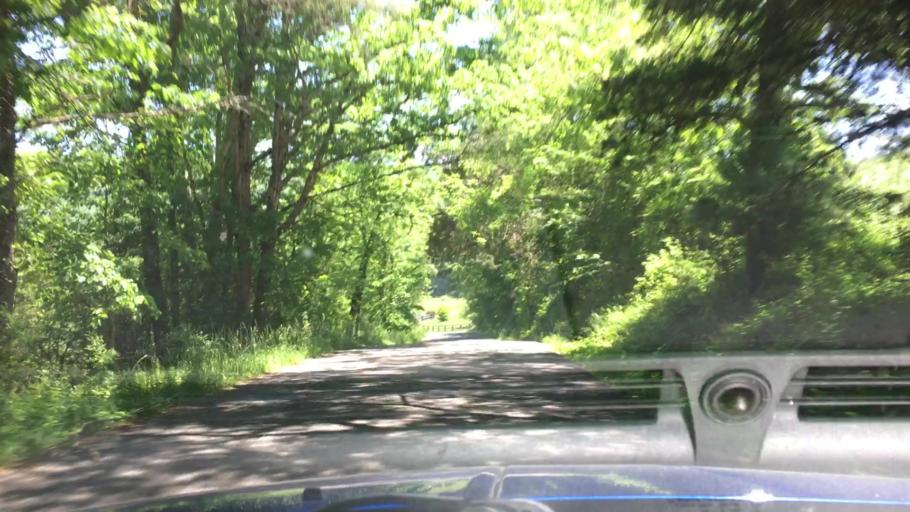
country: US
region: Virginia
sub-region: Bath County
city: Warm Springs
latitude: 38.0745
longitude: -79.5848
